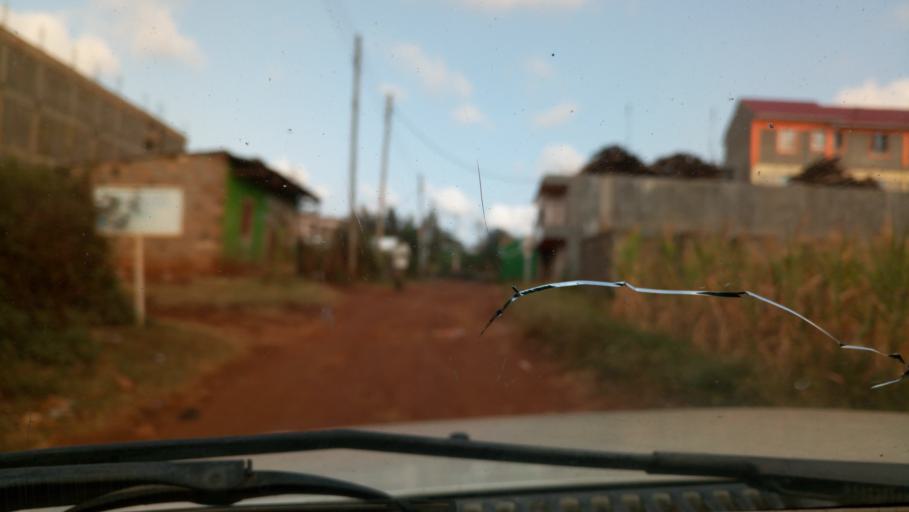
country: KE
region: Nairobi Area
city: Thika
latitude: -0.9329
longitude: 37.1250
